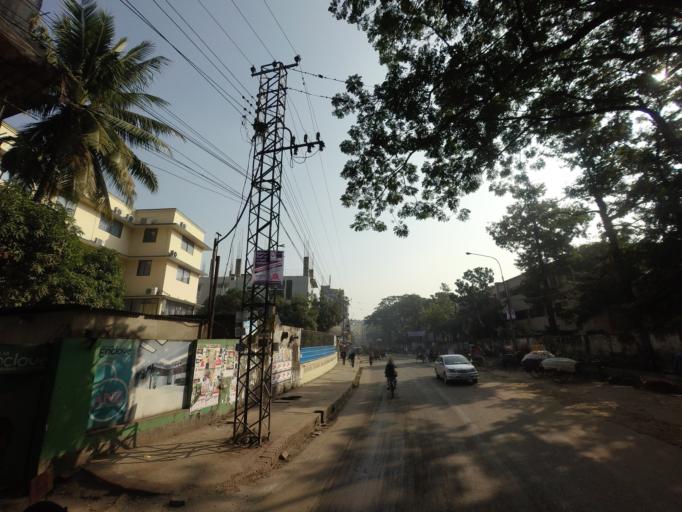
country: BD
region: Chittagong
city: Chittagong
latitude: 22.3595
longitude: 91.8341
